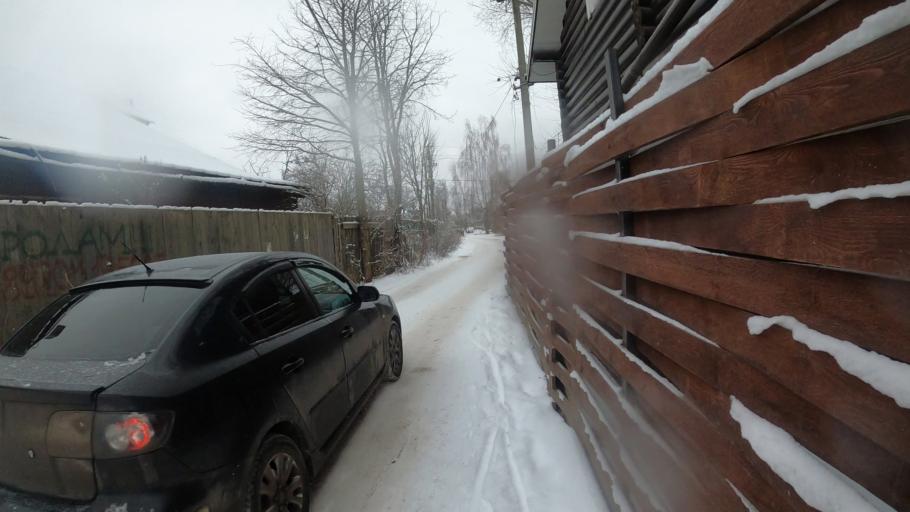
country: RU
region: Jaroslavl
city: Pereslavl'-Zalesskiy
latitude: 56.7341
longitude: 38.8345
